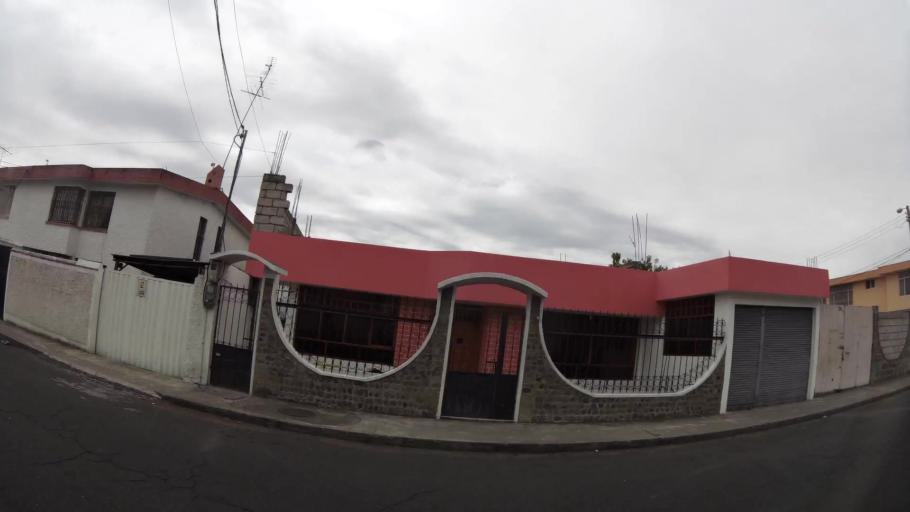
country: EC
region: Cotopaxi
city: Latacunga
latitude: -0.9453
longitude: -78.6131
